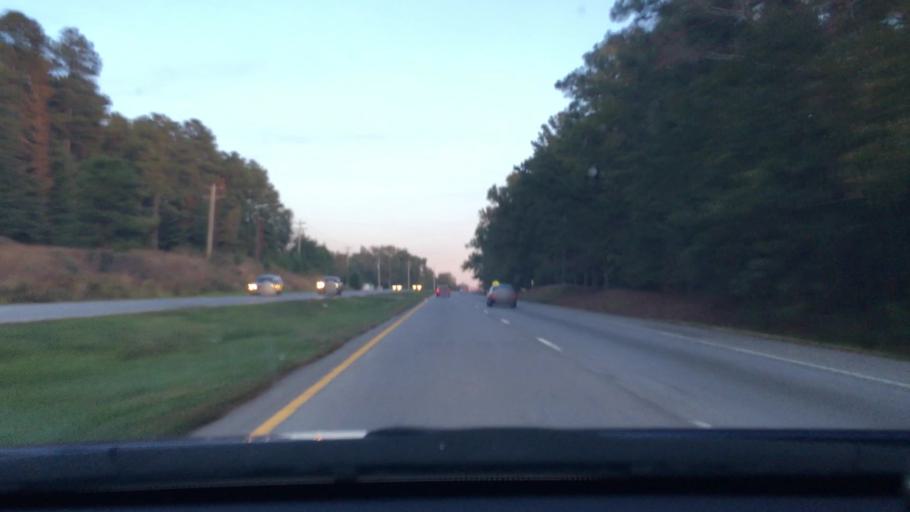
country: US
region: South Carolina
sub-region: Richland County
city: Gadsden
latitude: 33.9423
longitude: -80.7281
